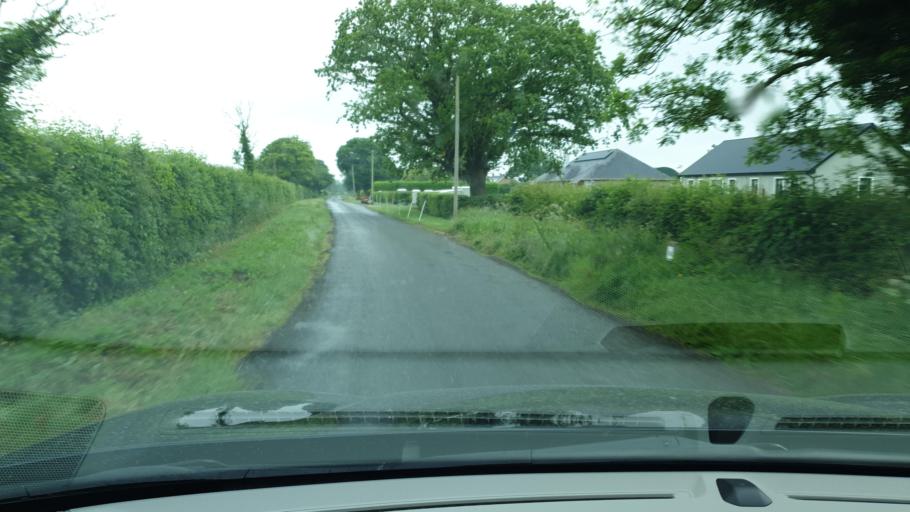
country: IE
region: Leinster
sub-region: An Mhi
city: Ashbourne
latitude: 53.4615
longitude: -6.4214
